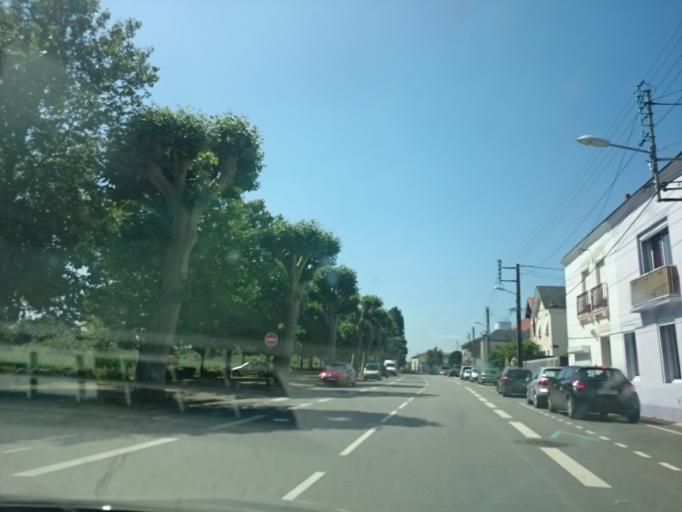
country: FR
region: Pays de la Loire
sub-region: Departement de la Loire-Atlantique
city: Indre
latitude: 47.2004
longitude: -1.6776
